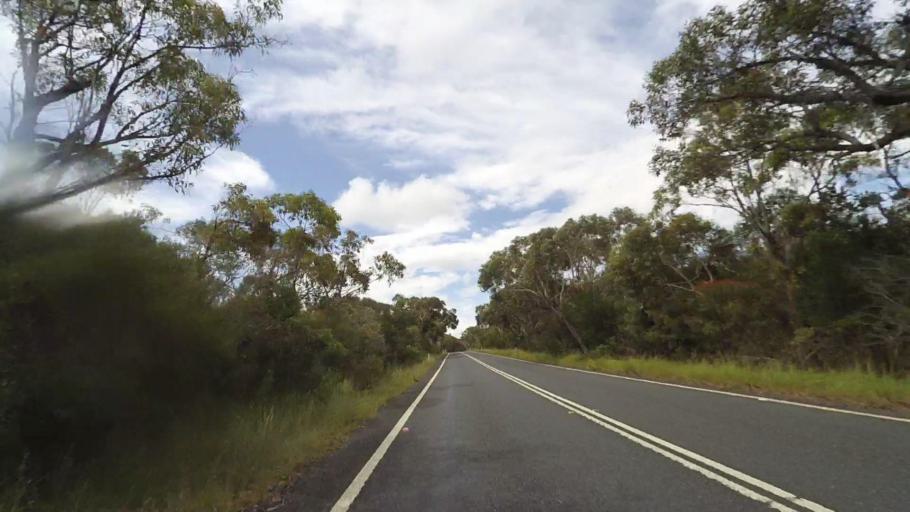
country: AU
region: New South Wales
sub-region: Sutherland Shire
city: Heathcote
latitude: -34.0995
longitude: 151.0590
